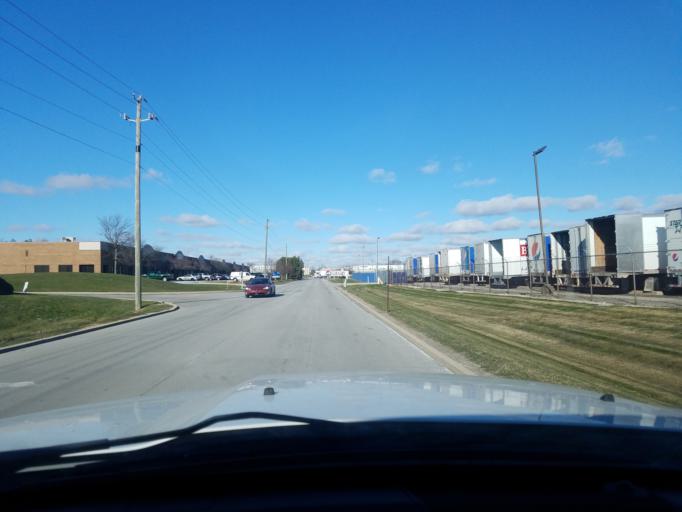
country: US
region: Indiana
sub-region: Boone County
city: Zionsville
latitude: 39.8915
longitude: -86.2562
